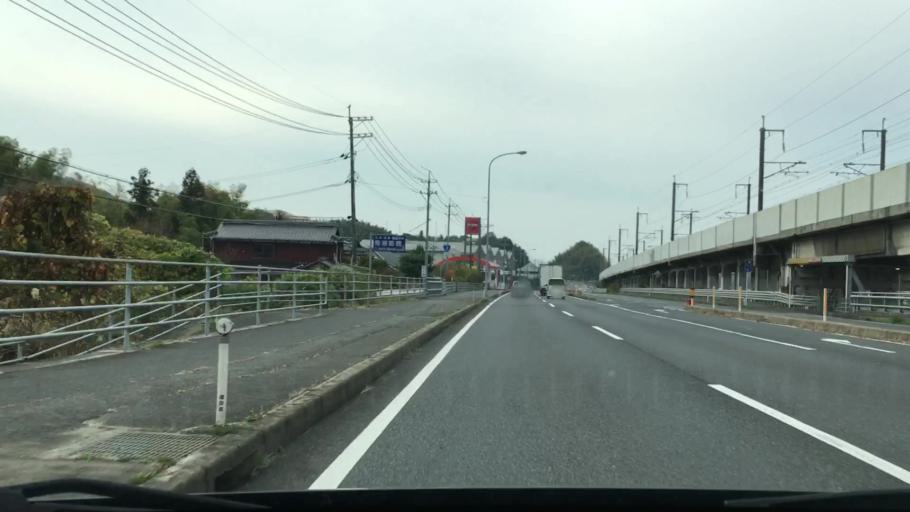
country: JP
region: Yamaguchi
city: Kudamatsu
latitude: 34.0347
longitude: 131.8844
